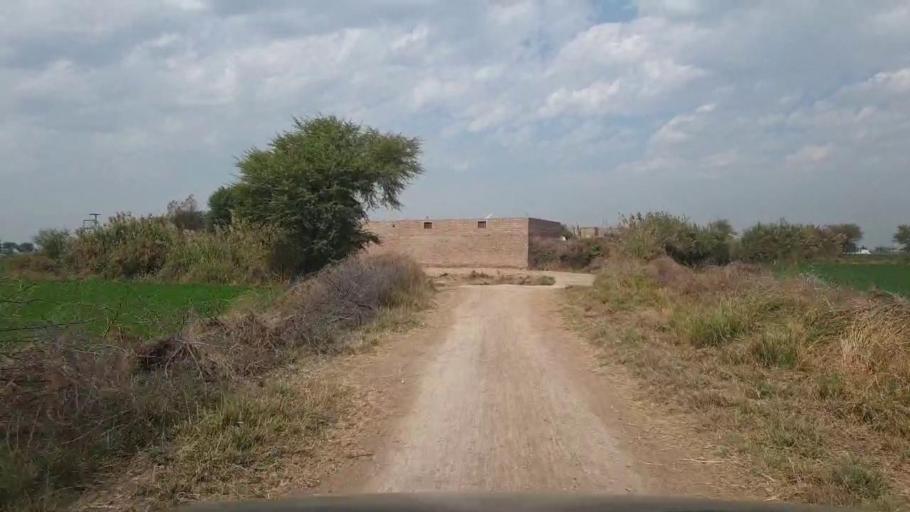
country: PK
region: Sindh
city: Sakrand
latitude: 26.0180
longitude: 68.3920
